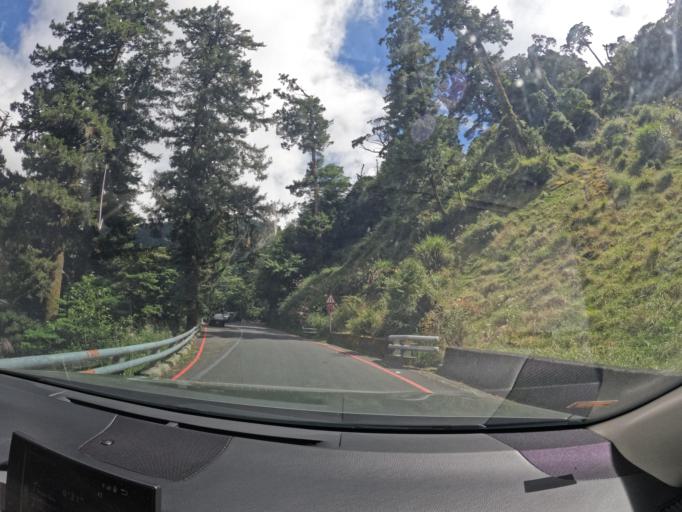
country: TW
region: Taiwan
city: Yujing
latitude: 23.2655
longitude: 120.9399
